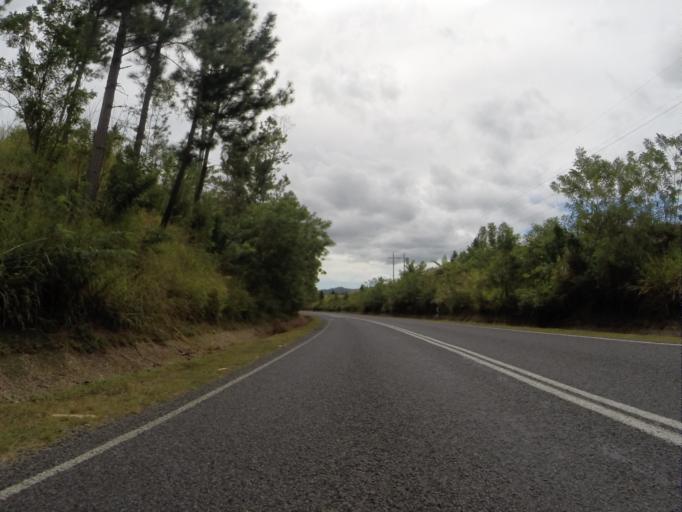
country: FJ
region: Western
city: Nadi
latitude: -17.9918
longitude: 177.3221
